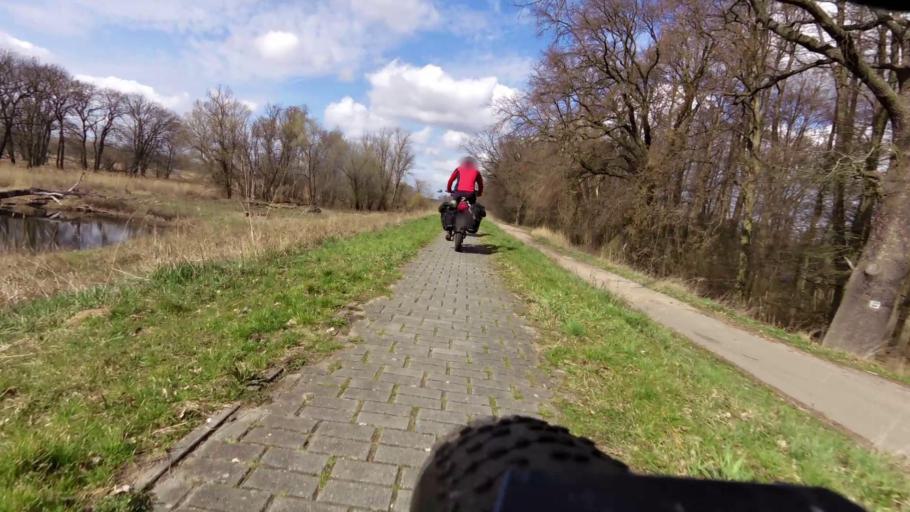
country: PL
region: Lubusz
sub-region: Powiat slubicki
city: Slubice
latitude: 52.3746
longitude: 14.5586
